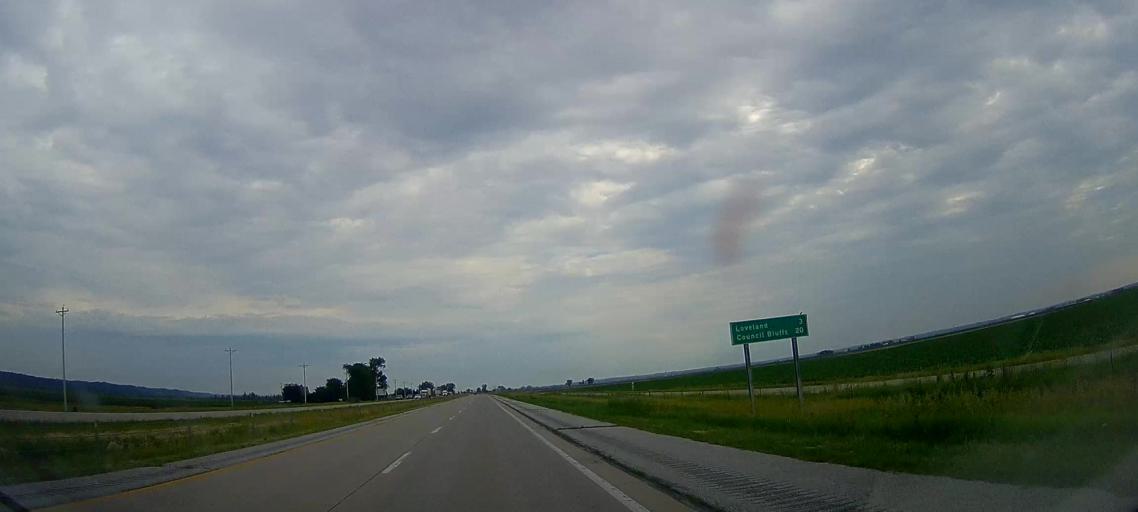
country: US
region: Iowa
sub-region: Harrison County
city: Missouri Valley
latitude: 41.5386
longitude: -95.9179
